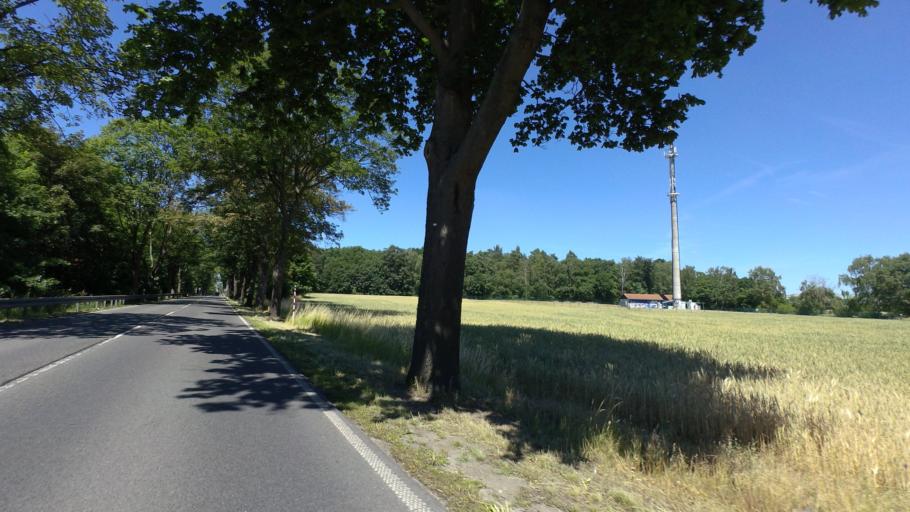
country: DE
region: Brandenburg
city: Rangsdorf
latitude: 52.2910
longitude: 13.4592
